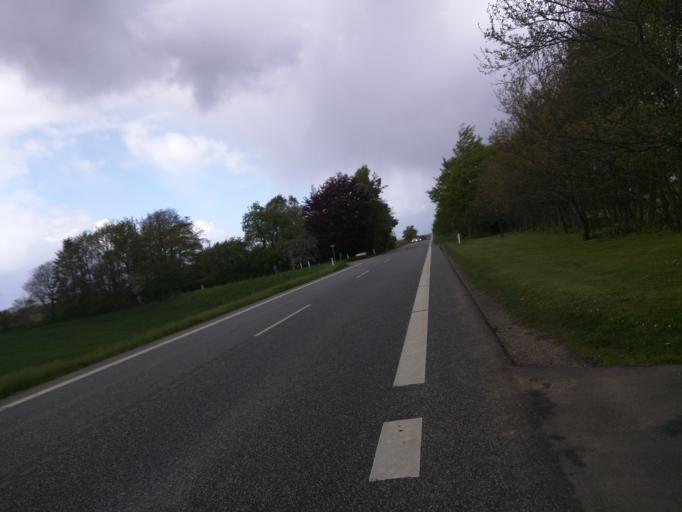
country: DK
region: Central Jutland
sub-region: Silkeborg Kommune
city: Kjellerup
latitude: 56.3532
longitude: 9.4349
